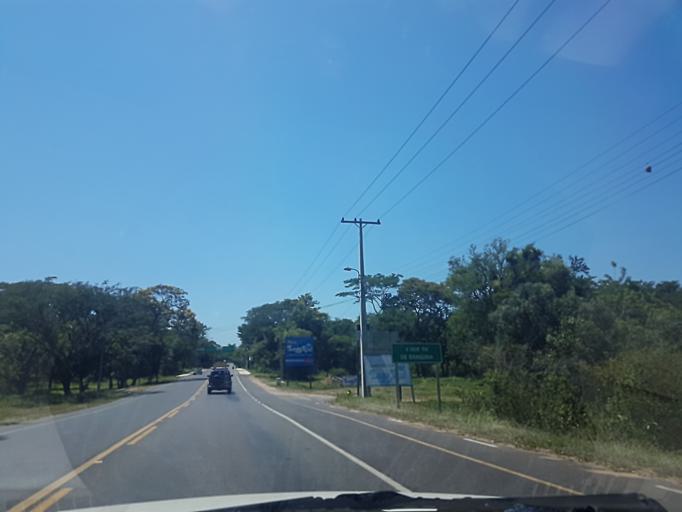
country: PY
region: Cordillera
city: San Bernardino
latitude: -25.2869
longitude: -57.3142
